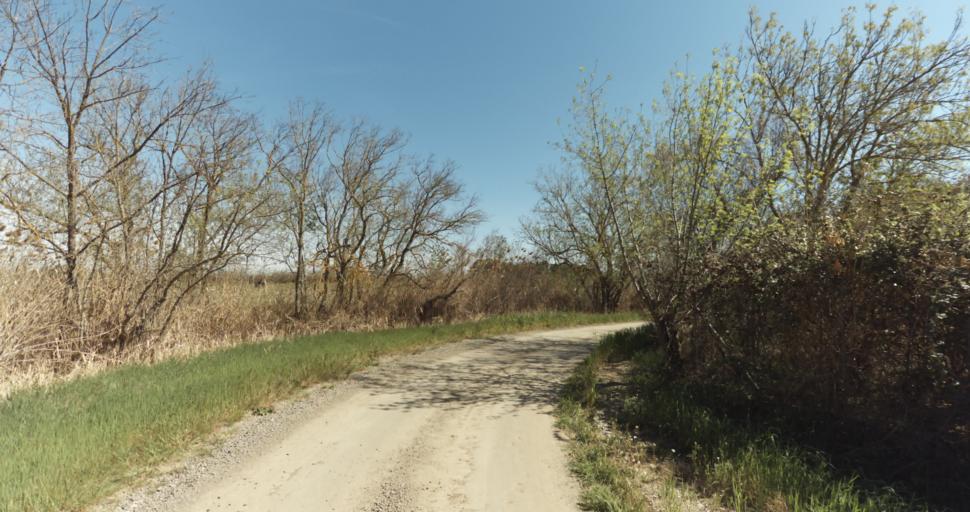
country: FR
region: Languedoc-Roussillon
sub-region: Departement de l'Herault
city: Marseillan
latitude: 43.3844
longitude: 3.5390
